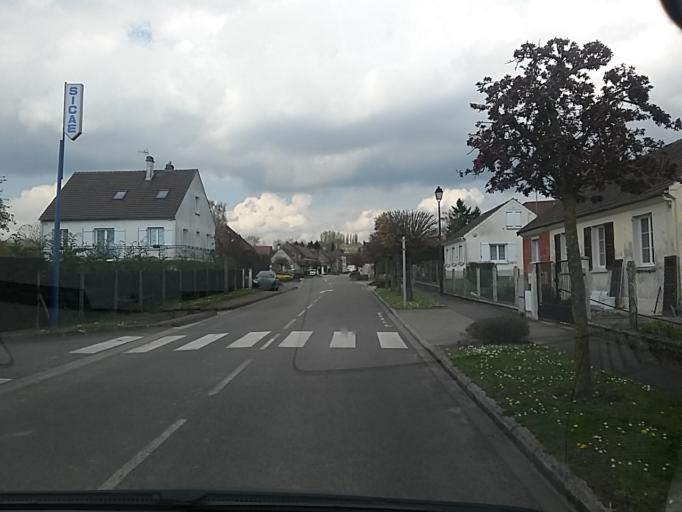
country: FR
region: Picardie
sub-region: Departement de l'Oise
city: Grandfresnoy
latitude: 49.3644
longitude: 2.6623
